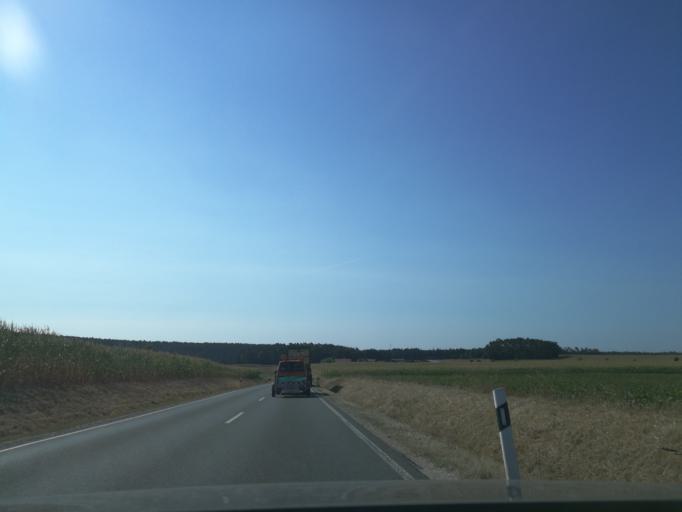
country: DE
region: Bavaria
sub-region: Regierungsbezirk Mittelfranken
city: Cadolzburg
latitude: 49.4422
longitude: 10.8496
